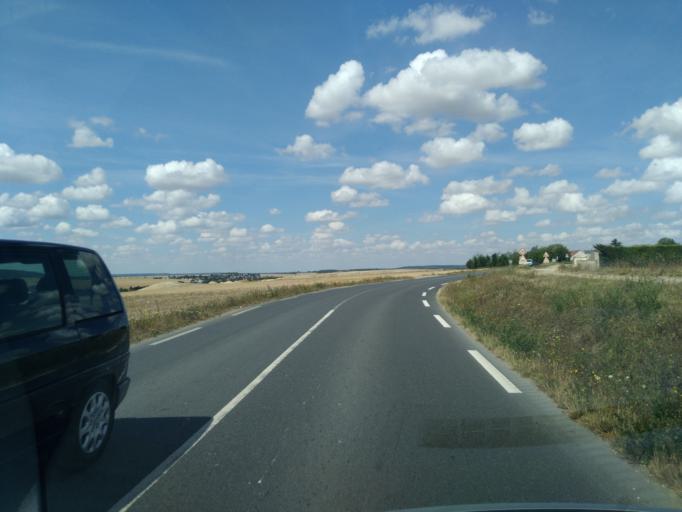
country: FR
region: Ile-de-France
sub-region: Departement des Yvelines
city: Plaisir
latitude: 48.8383
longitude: 1.9383
